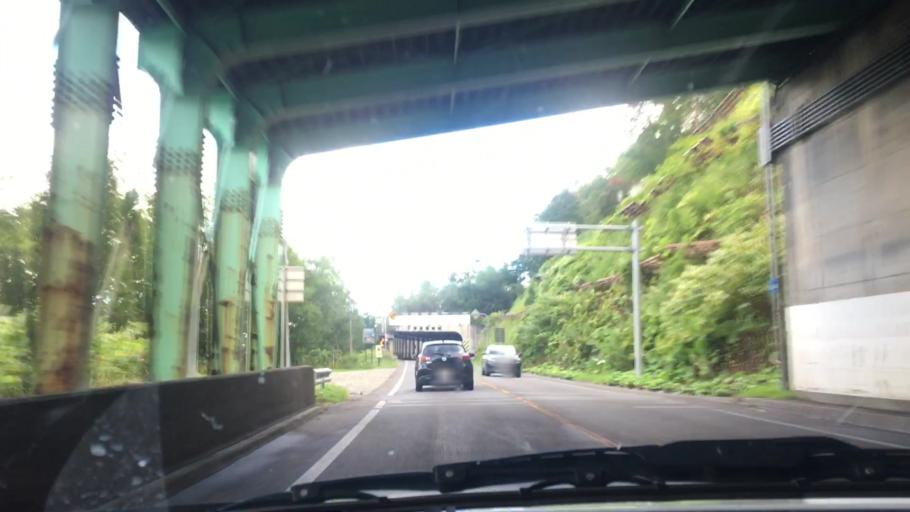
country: JP
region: Hokkaido
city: Shimo-furano
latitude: 43.1457
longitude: 142.7707
